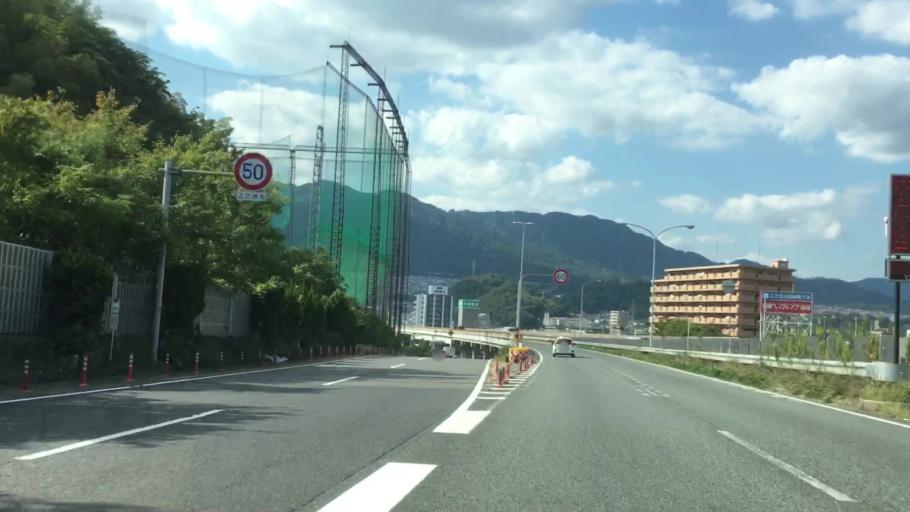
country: JP
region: Hiroshima
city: Hatsukaichi
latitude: 34.3783
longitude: 132.3651
